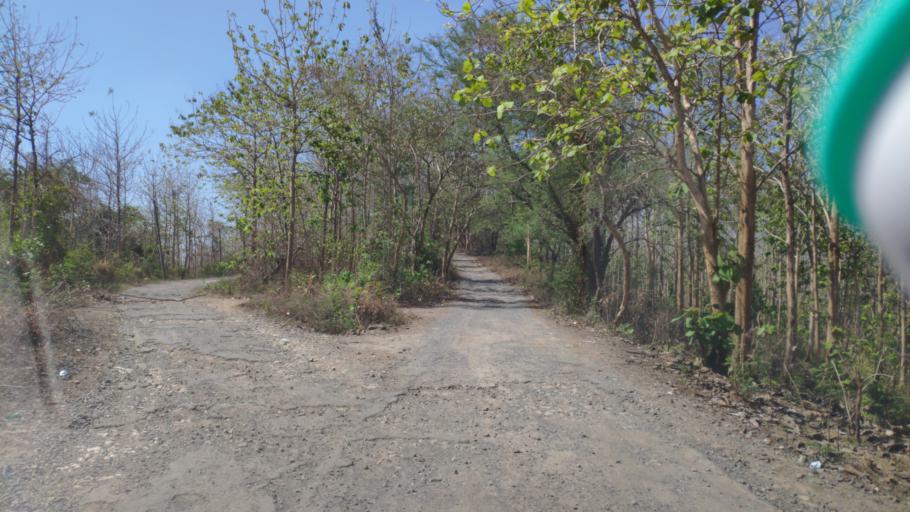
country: ID
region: East Java
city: Krajan Jamprong
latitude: -7.0025
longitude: 111.6056
